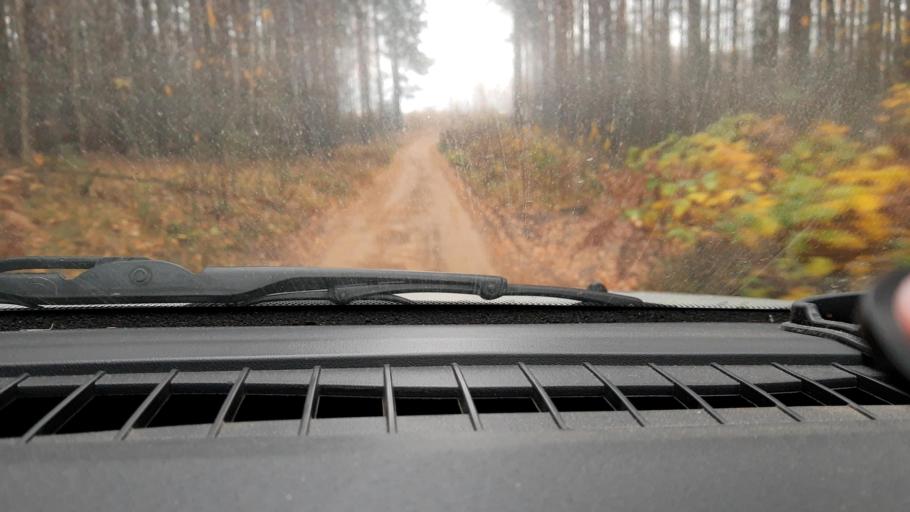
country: RU
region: Nizjnij Novgorod
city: Sitniki
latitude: 56.4331
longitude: 44.0663
